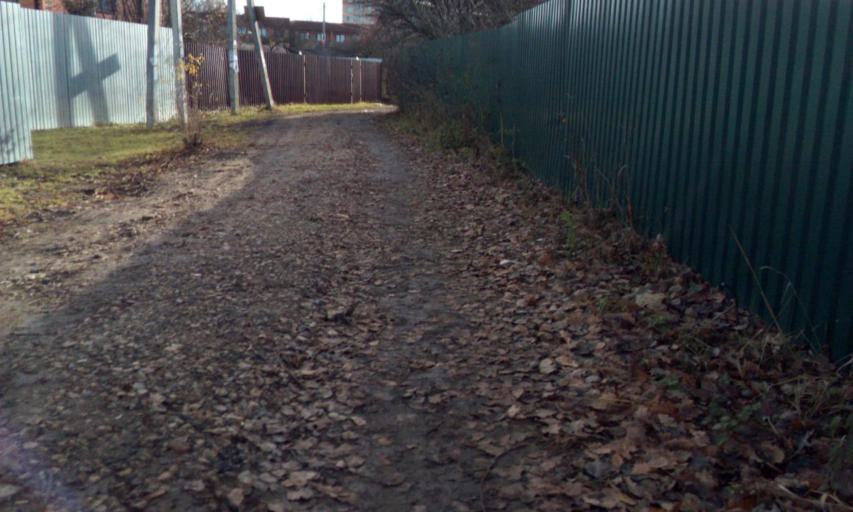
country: RU
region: Moskovskaya
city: Zhavoronki
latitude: 55.6578
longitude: 37.1525
